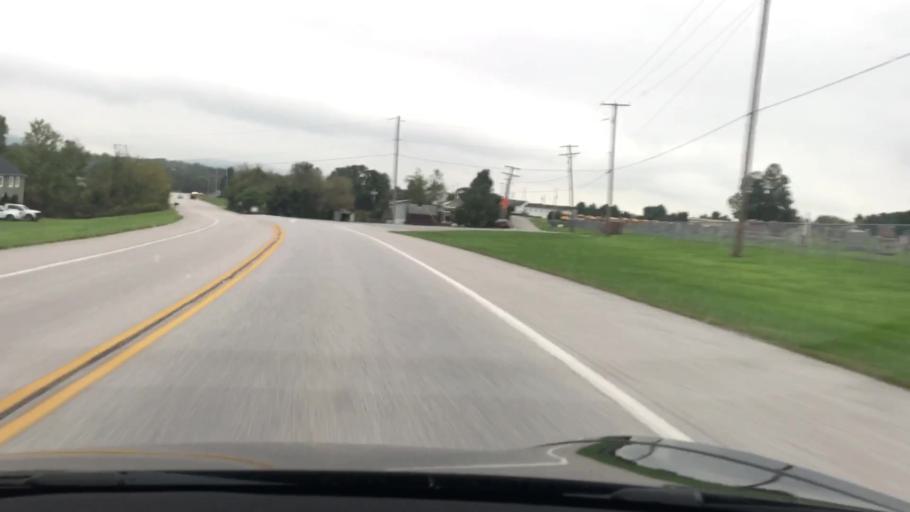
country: US
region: Pennsylvania
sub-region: York County
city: Dover
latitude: 39.9917
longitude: -76.8579
